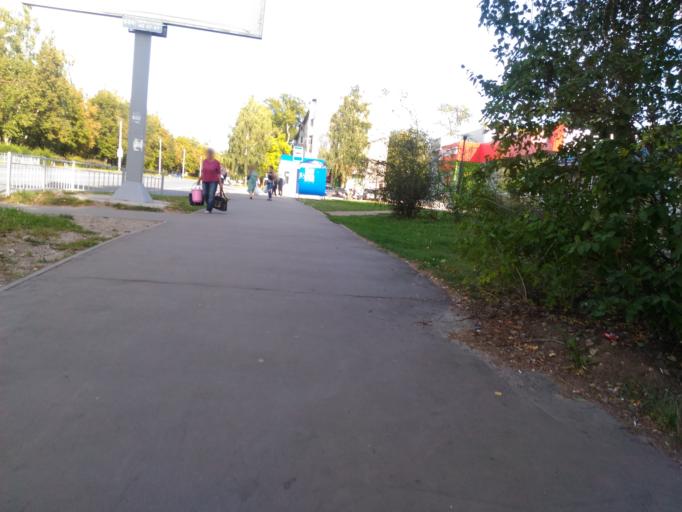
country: RU
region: Ulyanovsk
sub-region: Ulyanovskiy Rayon
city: Ulyanovsk
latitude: 54.3527
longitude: 48.5338
